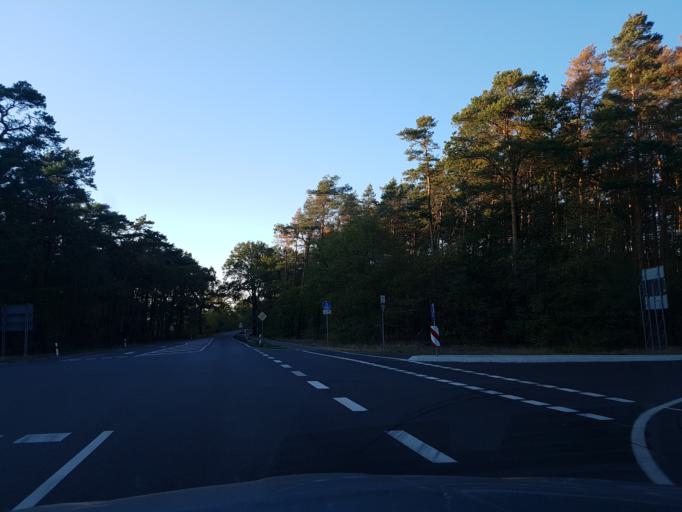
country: DE
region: Brandenburg
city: Bad Liebenwerda
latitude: 51.5520
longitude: 13.3794
